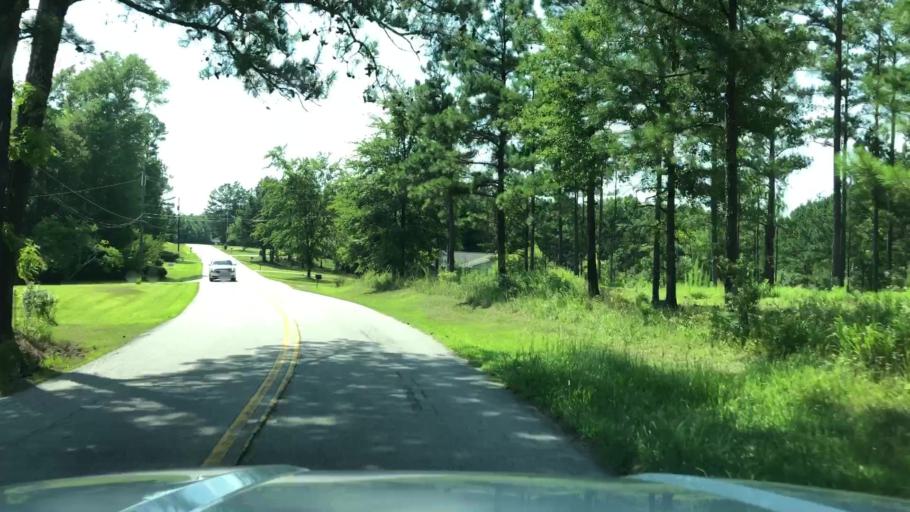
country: US
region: Georgia
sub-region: Paulding County
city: Dallas
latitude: 33.9479
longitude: -84.8440
